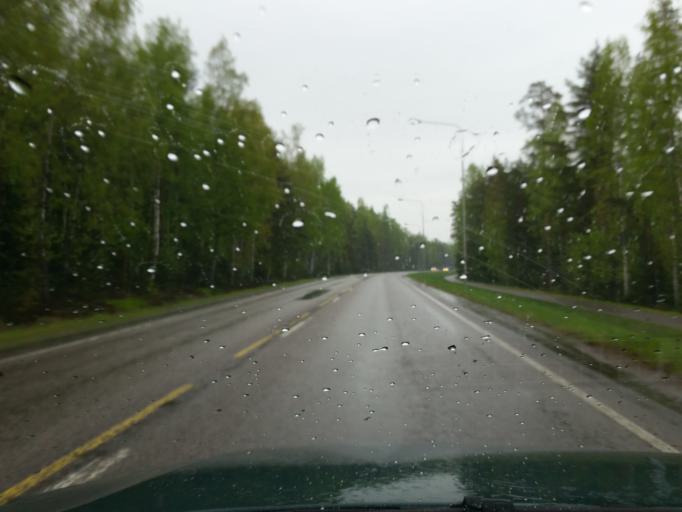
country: FI
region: Uusimaa
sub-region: Helsinki
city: Lohja
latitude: 60.2829
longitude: 24.1624
